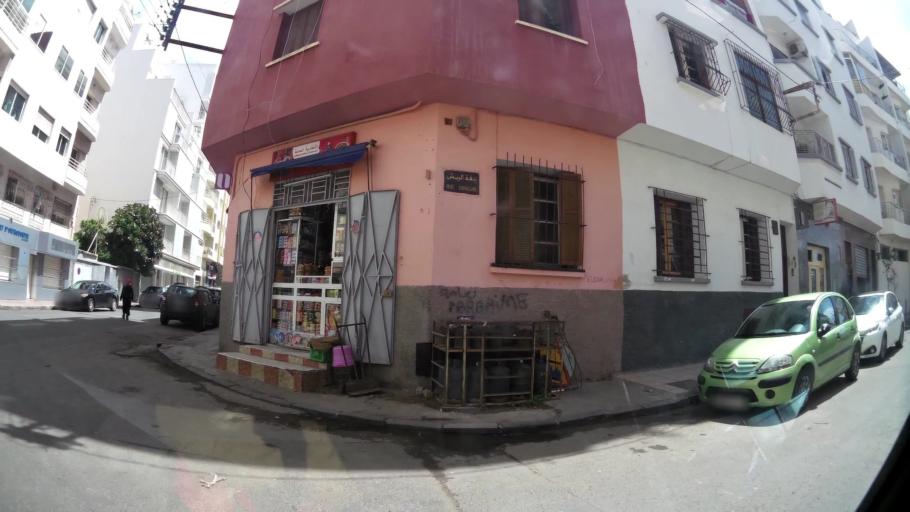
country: MA
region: Grand Casablanca
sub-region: Casablanca
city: Casablanca
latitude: 33.5973
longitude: -7.6365
